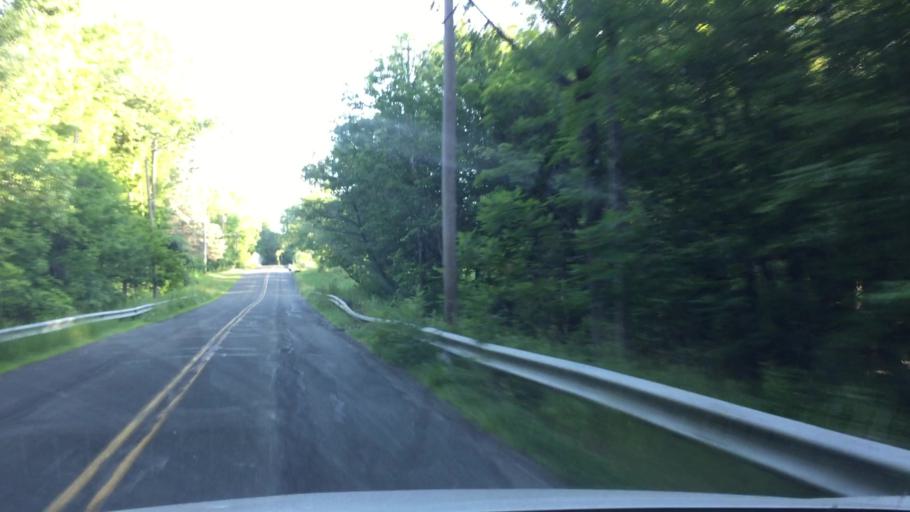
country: US
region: Massachusetts
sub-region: Berkshire County
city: Otis
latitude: 42.2469
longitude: -73.1120
